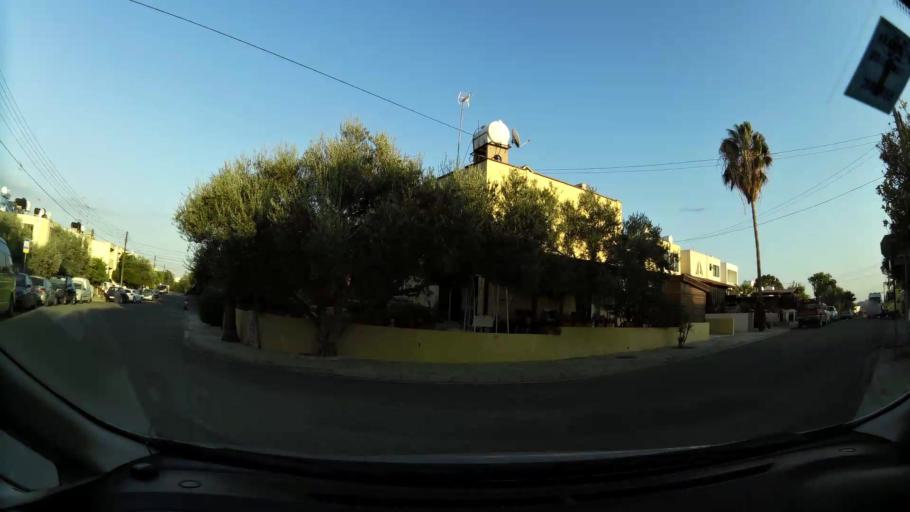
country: CY
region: Larnaka
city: Larnaca
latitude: 34.9157
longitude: 33.5916
